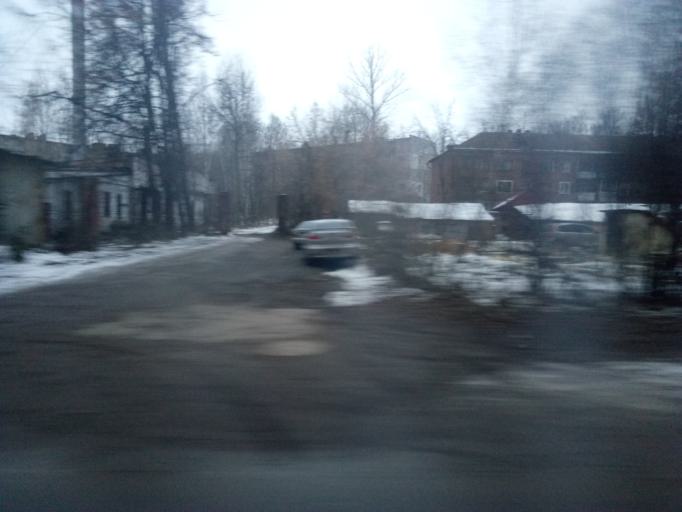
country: RU
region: Tula
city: Tula
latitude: 54.1967
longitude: 37.5627
